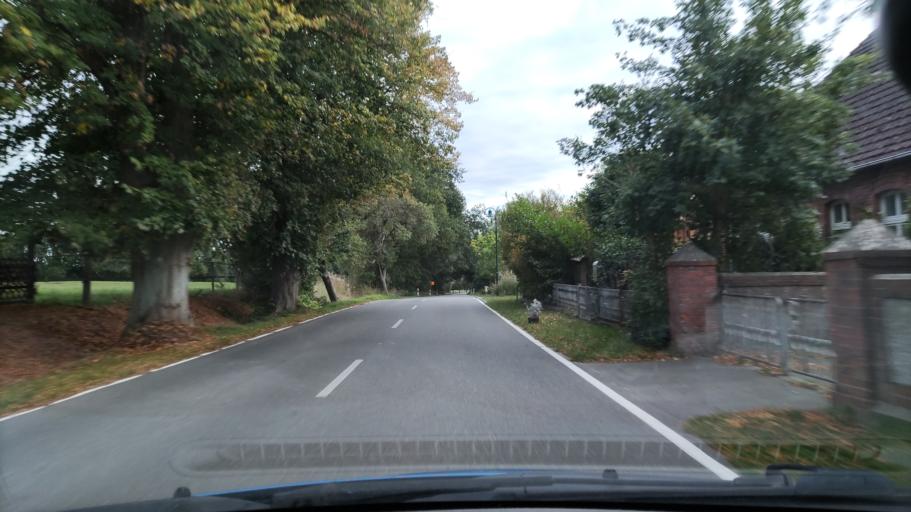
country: DE
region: Mecklenburg-Vorpommern
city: Boizenburg
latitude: 53.4254
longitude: 10.8407
